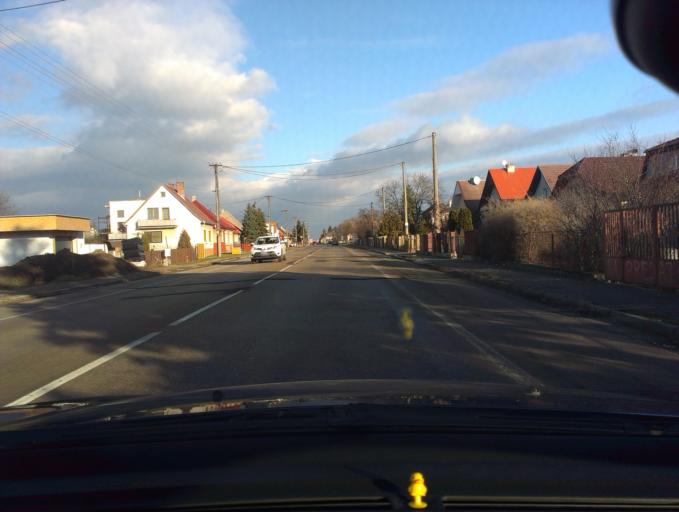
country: SK
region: Trnavsky
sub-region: Okres Trnava
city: Piestany
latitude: 48.6540
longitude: 17.8404
